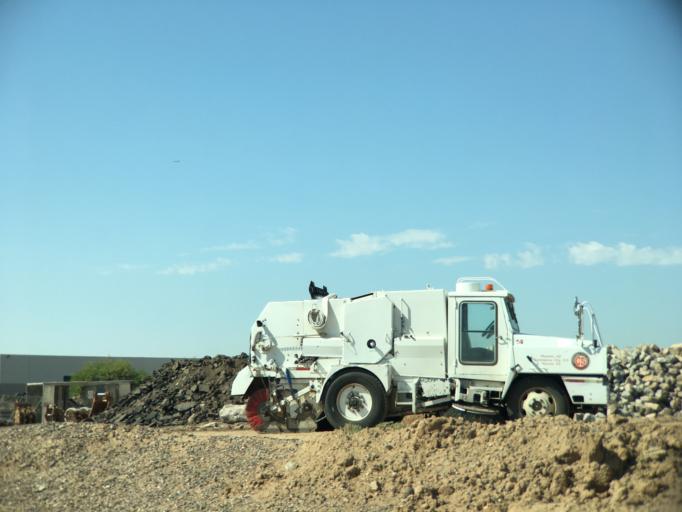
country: US
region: Arizona
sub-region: Maricopa County
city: Glendale
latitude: 33.4618
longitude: -112.1822
